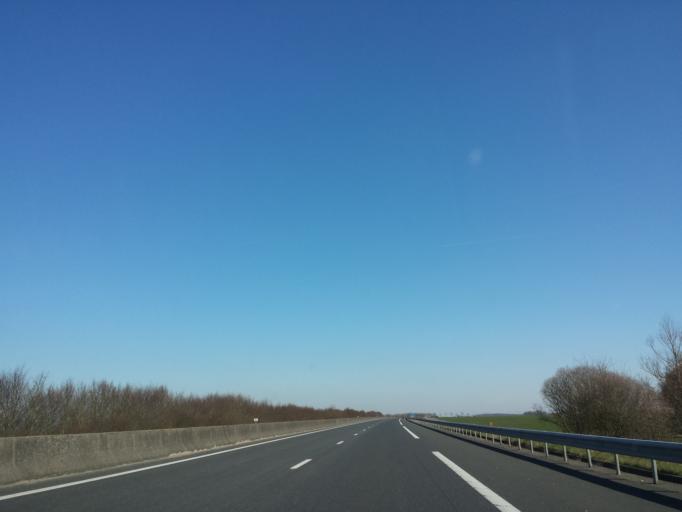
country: FR
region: Picardie
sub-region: Departement de l'Oise
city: Tille
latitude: 49.5060
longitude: 2.1770
